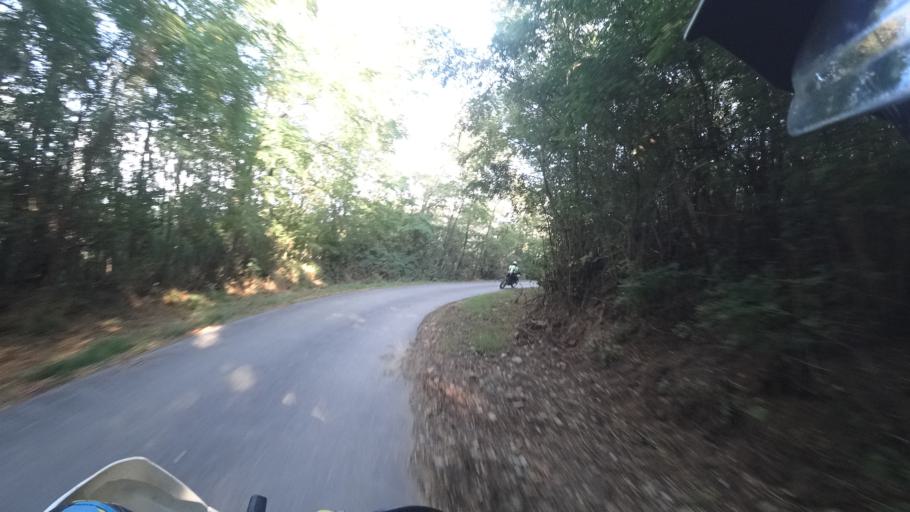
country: HR
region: Sibensko-Kniniska
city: Knin
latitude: 44.1326
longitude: 16.1356
